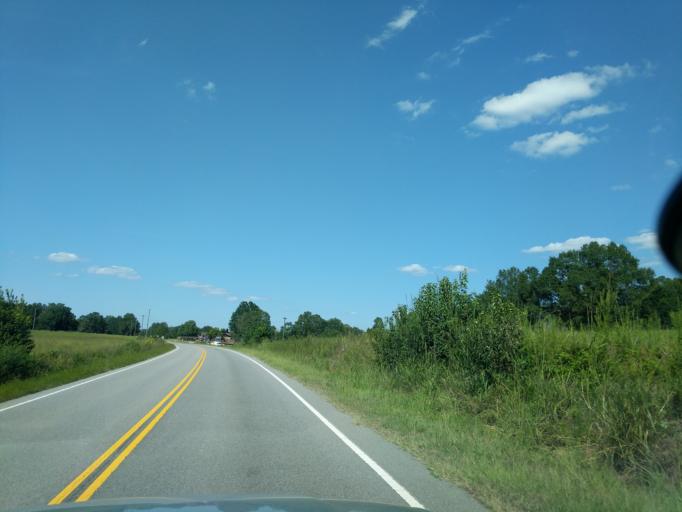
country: US
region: South Carolina
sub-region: Newberry County
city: Prosperity
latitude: 34.1286
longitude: -81.5424
